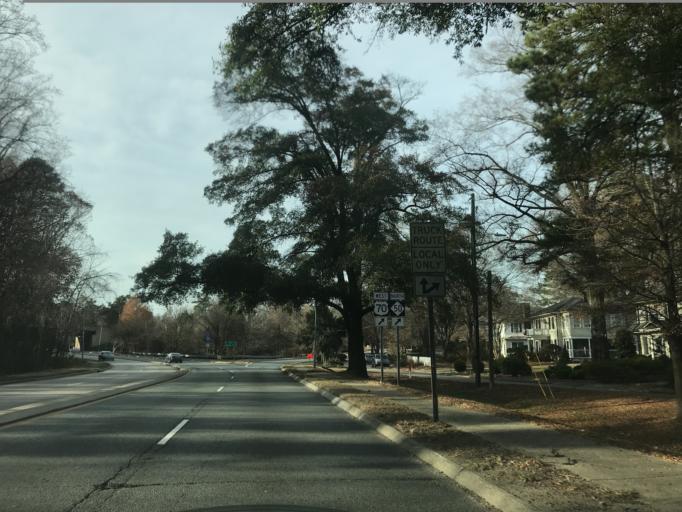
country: US
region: North Carolina
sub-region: Wake County
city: West Raleigh
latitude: 35.7975
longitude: -78.6441
